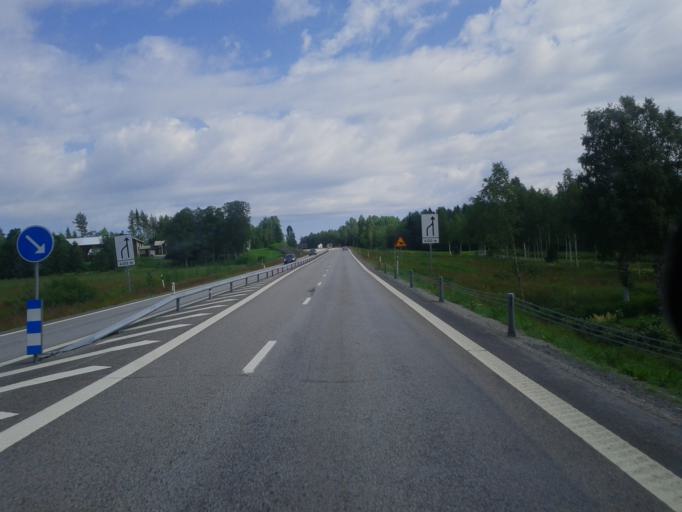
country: SE
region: Vaesternorrland
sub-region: OErnskoeldsviks Kommun
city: Ornskoldsvik
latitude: 63.2968
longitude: 18.8887
